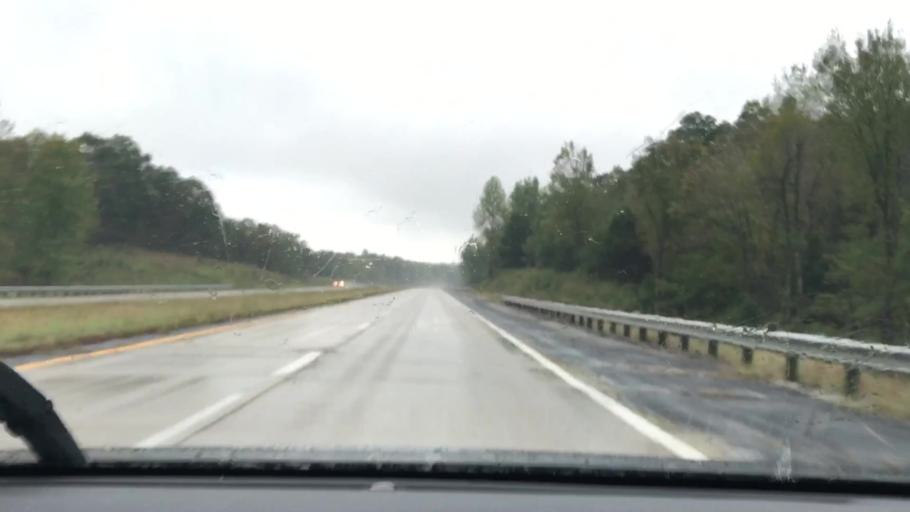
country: US
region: Kentucky
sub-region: Hopkins County
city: Nortonville
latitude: 37.1375
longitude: -87.4604
